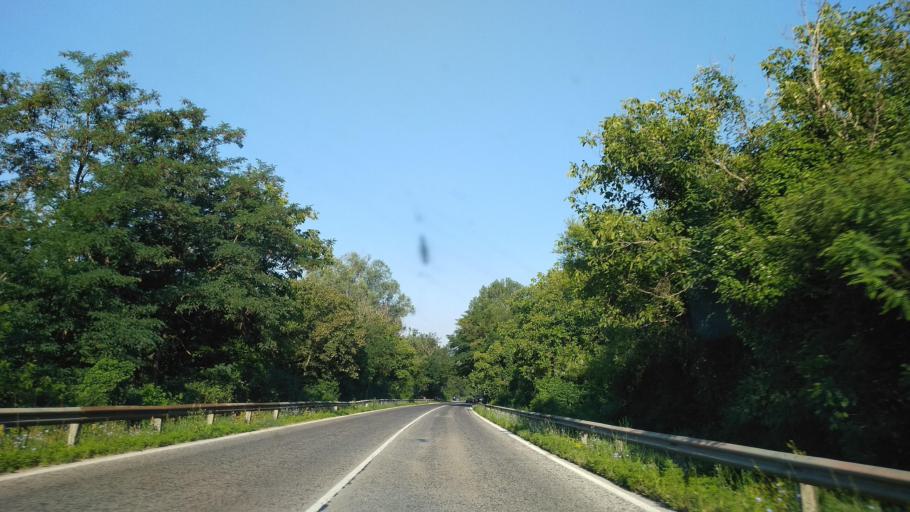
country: BG
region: Lovech
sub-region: Obshtina Lovech
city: Lovech
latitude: 43.0407
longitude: 24.7326
